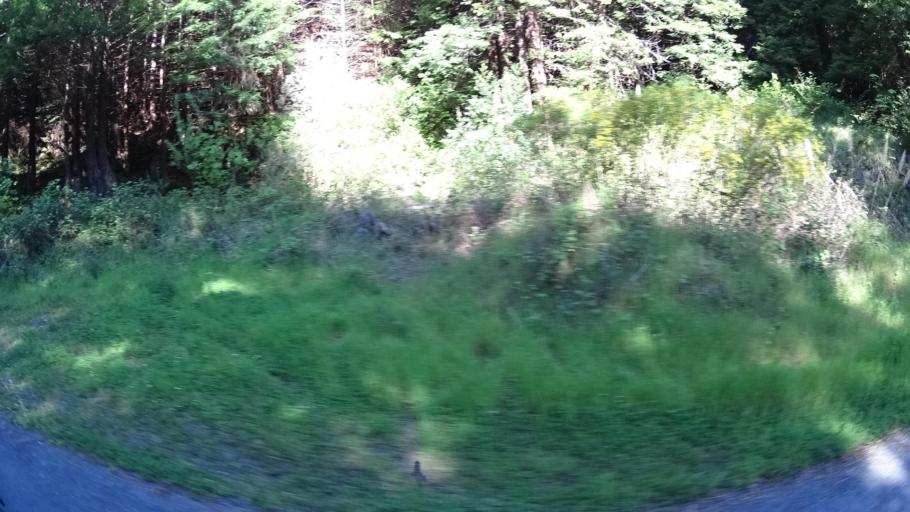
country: US
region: California
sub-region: Humboldt County
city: Rio Dell
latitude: 40.4639
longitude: -124.0542
